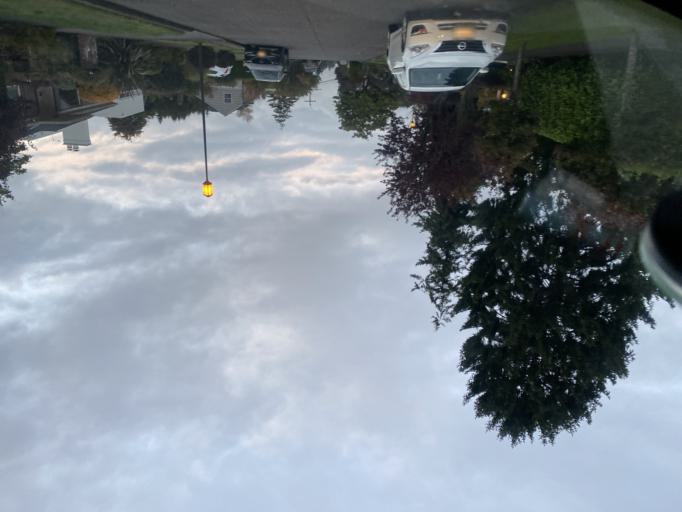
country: US
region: Washington
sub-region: King County
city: Seattle
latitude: 47.6346
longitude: -122.3958
